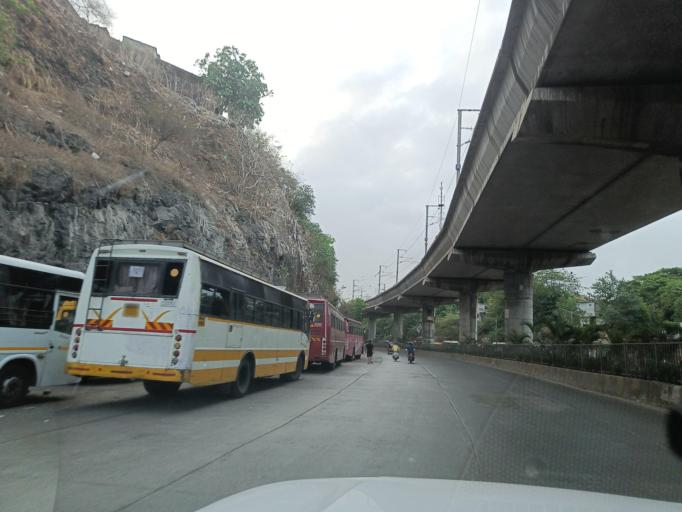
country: IN
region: Maharashtra
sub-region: Mumbai Suburban
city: Powai
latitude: 19.0915
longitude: 72.9043
